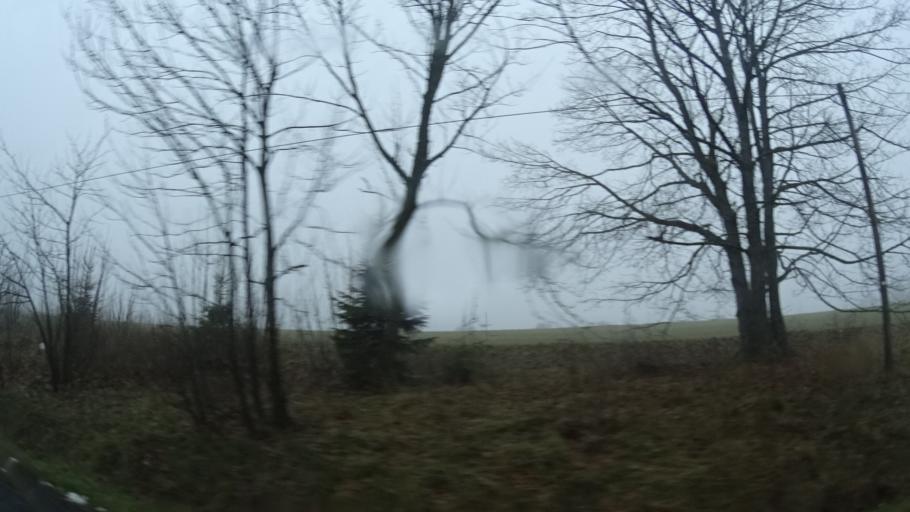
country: DE
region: Thuringia
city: Eisfeld
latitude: 50.5010
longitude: 10.9033
